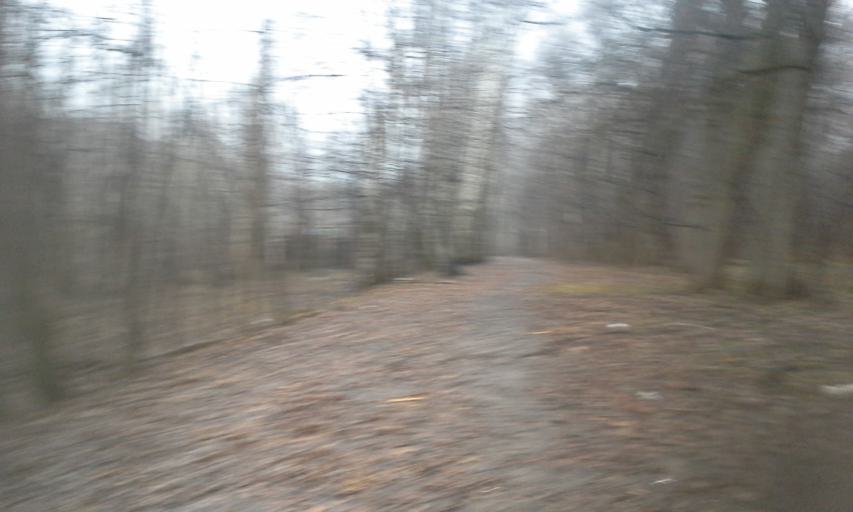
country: RU
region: Moscow
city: Chertanovo Yuzhnoye
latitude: 55.5995
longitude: 37.5601
